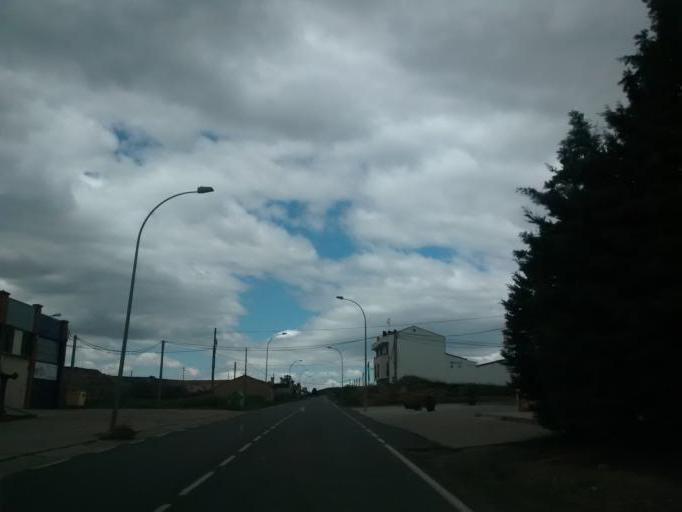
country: ES
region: La Rioja
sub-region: Provincia de La Rioja
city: Pradejon
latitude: 42.3368
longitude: -2.0753
